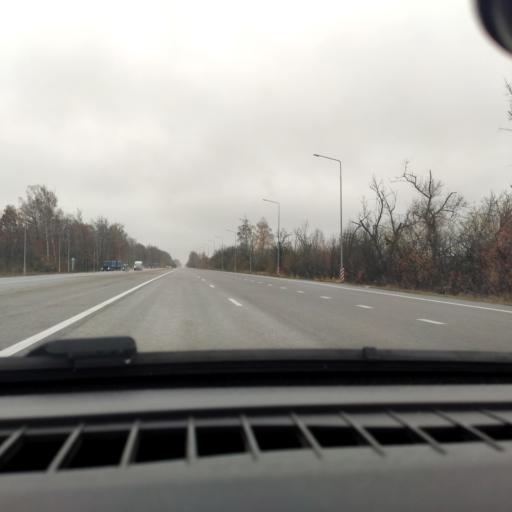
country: RU
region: Voronezj
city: Kolodeznyy
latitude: 51.3415
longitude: 39.0239
